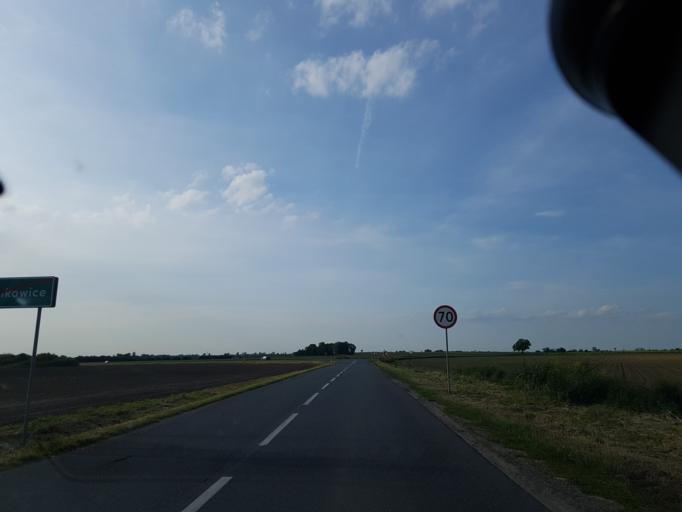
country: PL
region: Lower Silesian Voivodeship
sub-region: Powiat wroclawski
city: Kobierzyce
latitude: 50.9350
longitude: 16.9382
